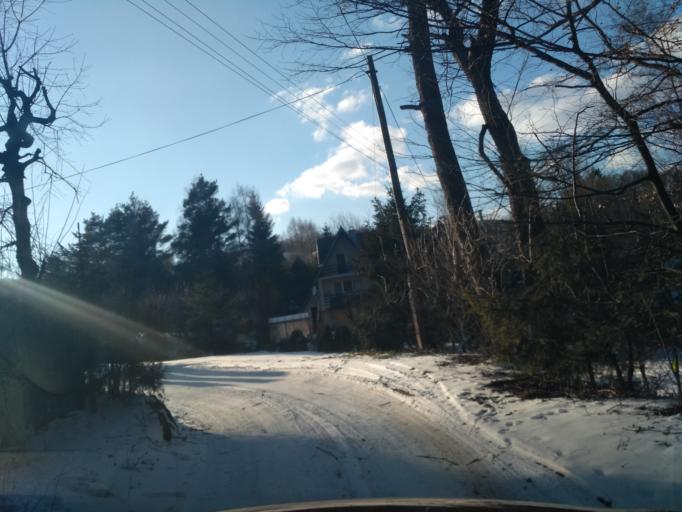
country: SK
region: Kosicky
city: Kosice
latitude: 48.7345
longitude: 21.1577
